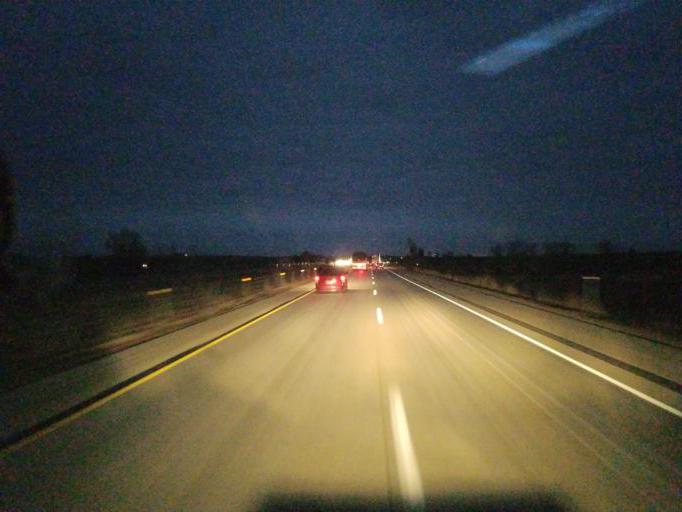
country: US
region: Iowa
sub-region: Guthrie County
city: Guthrie Center
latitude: 41.4934
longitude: -94.5971
